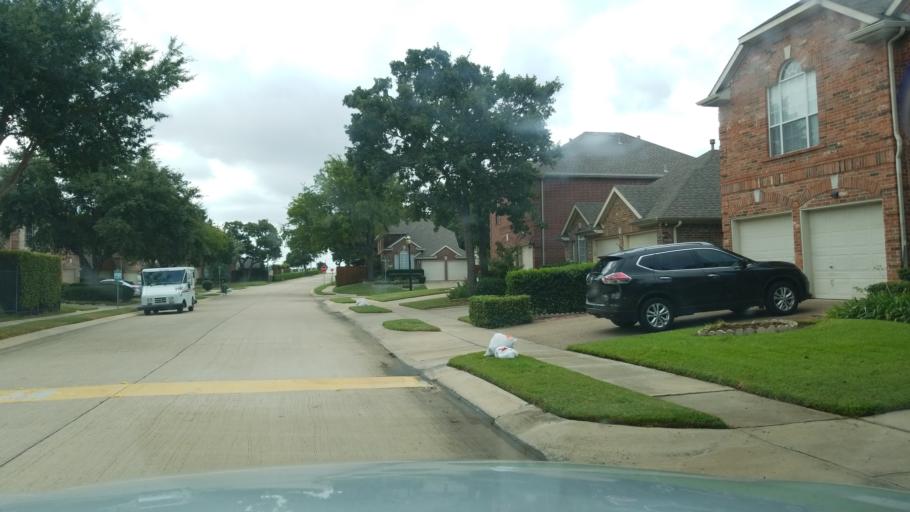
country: US
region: Texas
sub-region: Tarrant County
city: Euless
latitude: 32.8393
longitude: -97.1040
